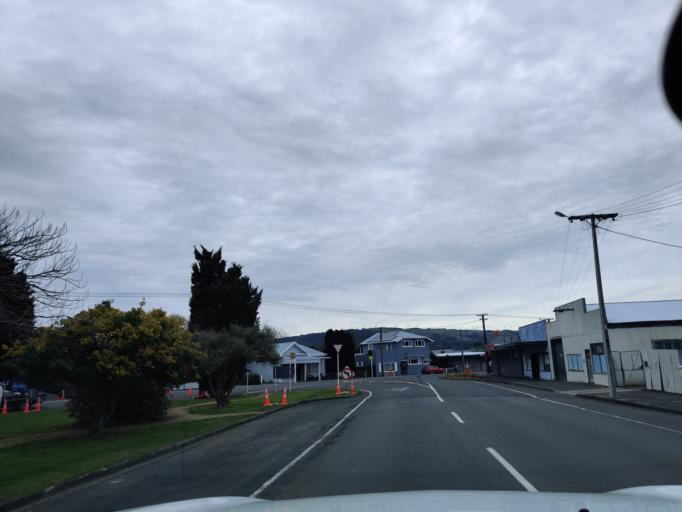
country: NZ
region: Manawatu-Wanganui
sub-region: Palmerston North City
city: Palmerston North
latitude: -40.2890
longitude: 175.7548
